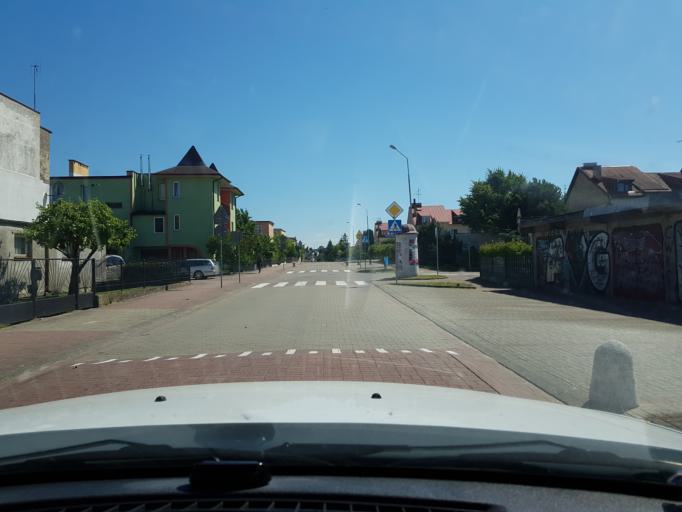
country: PL
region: West Pomeranian Voivodeship
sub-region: Powiat koszalinski
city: Mielno
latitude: 54.2551
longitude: 16.0595
